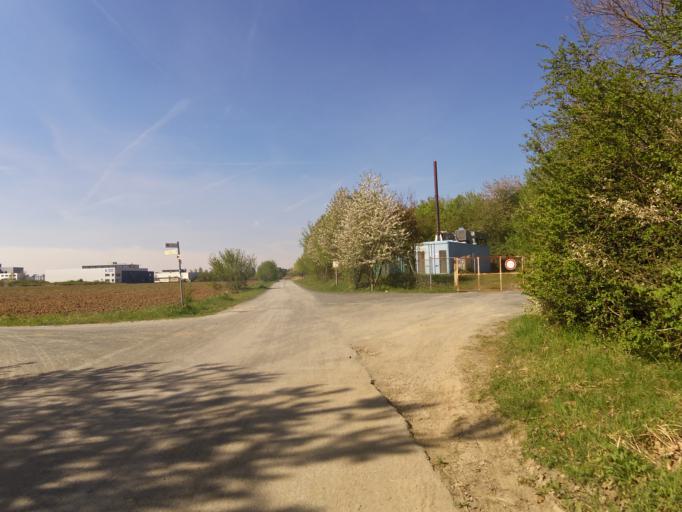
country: DE
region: Hesse
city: Morfelden-Walldorf
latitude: 49.9852
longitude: 8.5918
